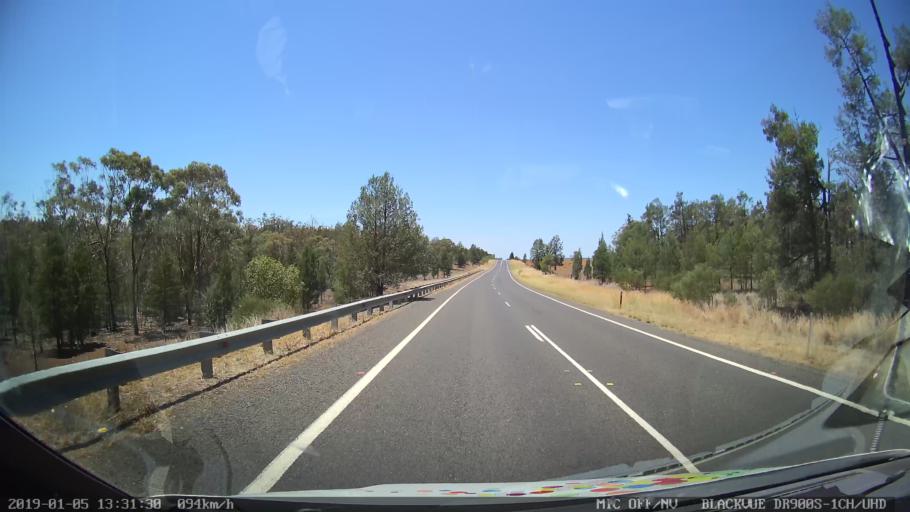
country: AU
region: New South Wales
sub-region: Gunnedah
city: Gunnedah
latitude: -31.0104
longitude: 150.0850
